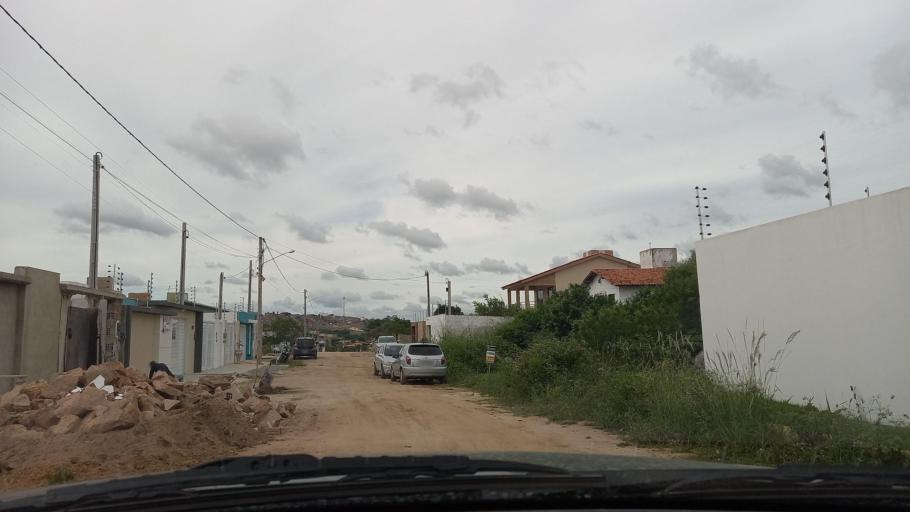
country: BR
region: Pernambuco
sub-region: Gravata
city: Gravata
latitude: -8.2246
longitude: -35.5759
